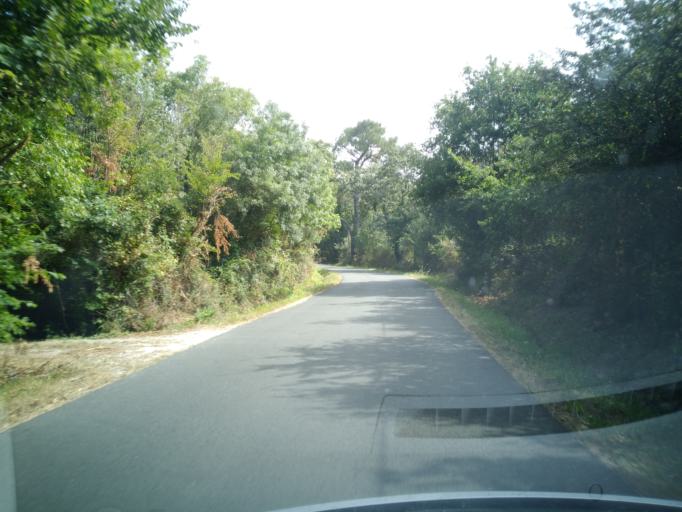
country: FR
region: Poitou-Charentes
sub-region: Departement de la Charente-Maritime
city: Chaillevette
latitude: 45.7170
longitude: -1.0758
